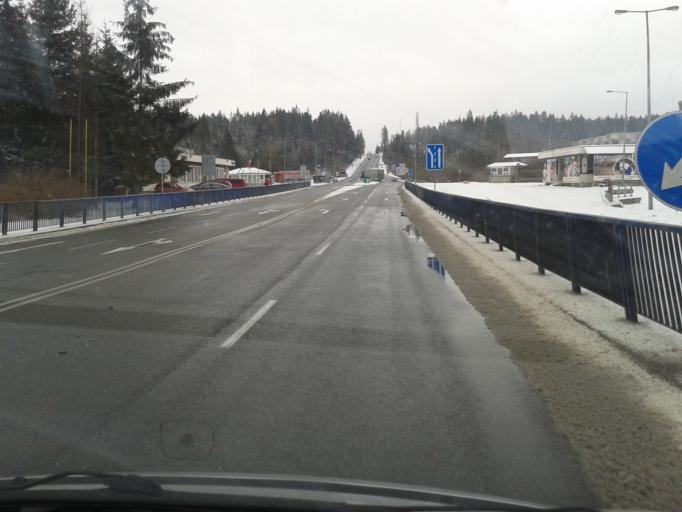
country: PL
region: Lesser Poland Voivodeship
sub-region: Powiat nowotarski
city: Chyzne
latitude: 49.4063
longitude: 19.6571
